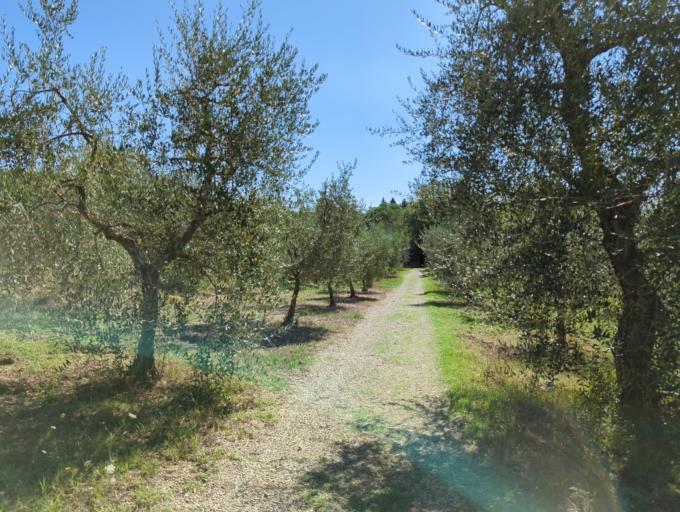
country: IT
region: Tuscany
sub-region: Province of Arezzo
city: Castiglion Fibocchi
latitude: 43.5276
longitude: 11.7815
